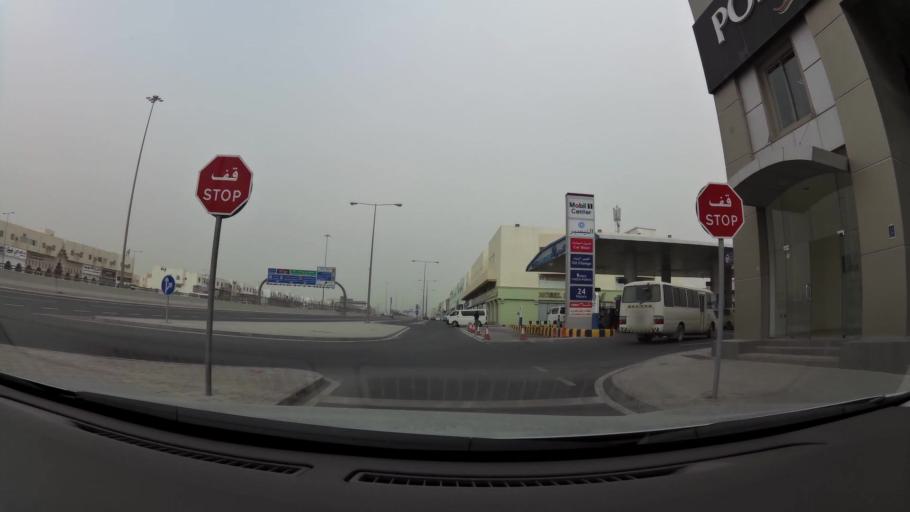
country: QA
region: Baladiyat ad Dawhah
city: Doha
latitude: 25.2580
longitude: 51.4876
